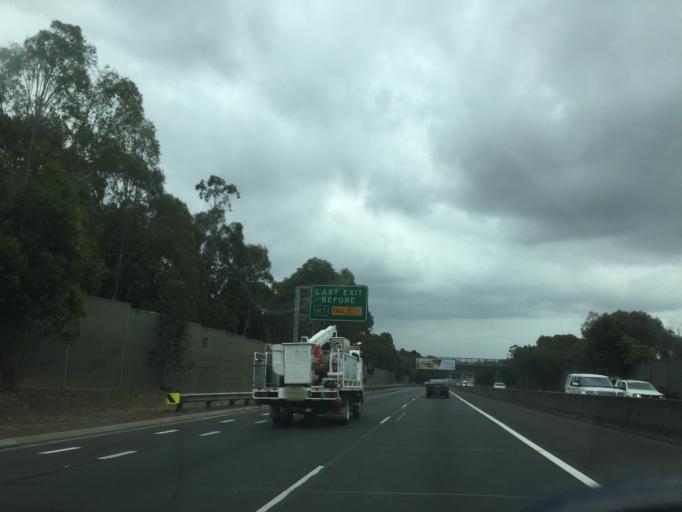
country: AU
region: New South Wales
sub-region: Parramatta
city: Northmead
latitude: -33.7720
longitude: 150.9815
